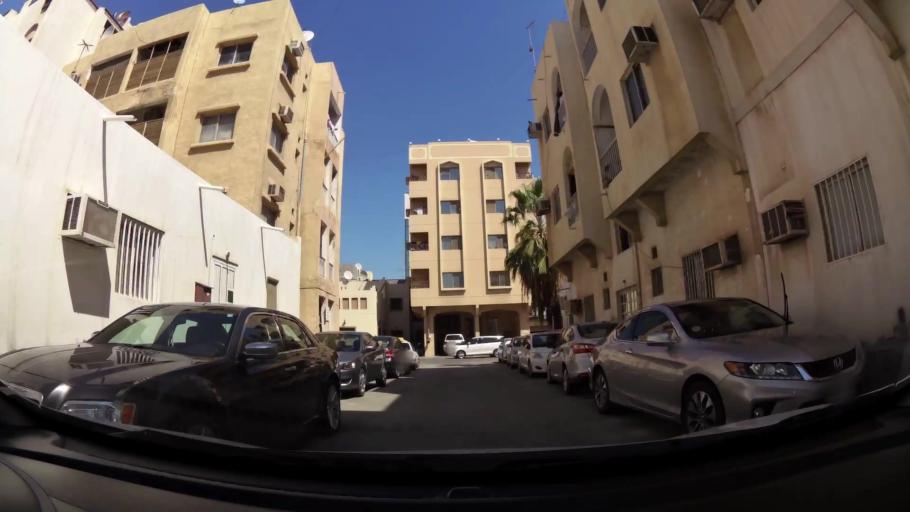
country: BH
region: Manama
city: Manama
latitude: 26.2010
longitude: 50.5955
